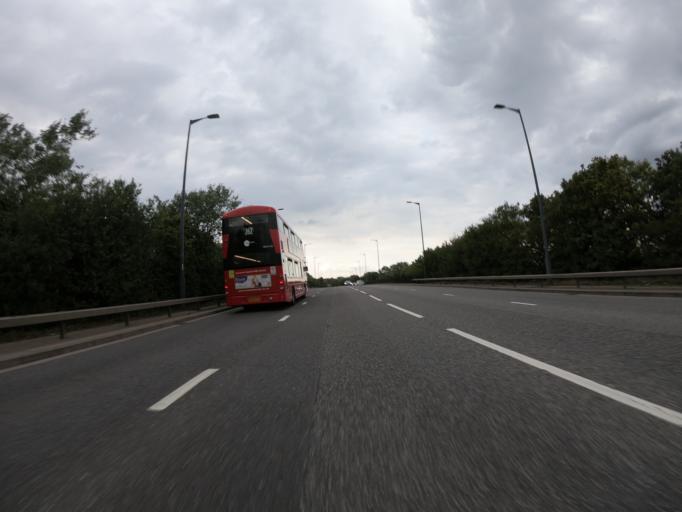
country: GB
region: England
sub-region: Greater London
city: Barking
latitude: 51.5181
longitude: 0.0729
